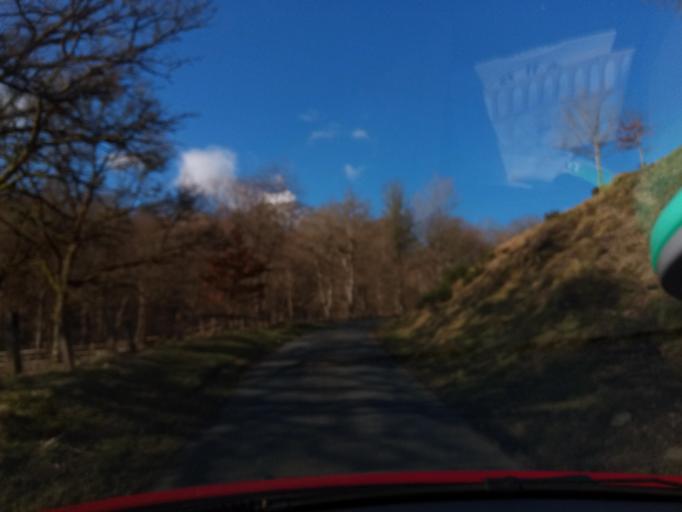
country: GB
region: Scotland
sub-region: The Scottish Borders
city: Hawick
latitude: 55.4228
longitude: -2.8711
